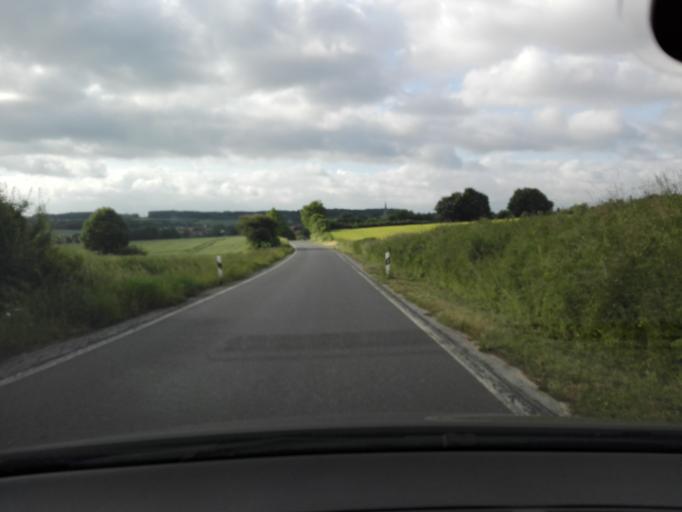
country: DE
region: North Rhine-Westphalia
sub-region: Regierungsbezirk Arnsberg
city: Frondenberg
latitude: 51.5100
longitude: 7.7348
